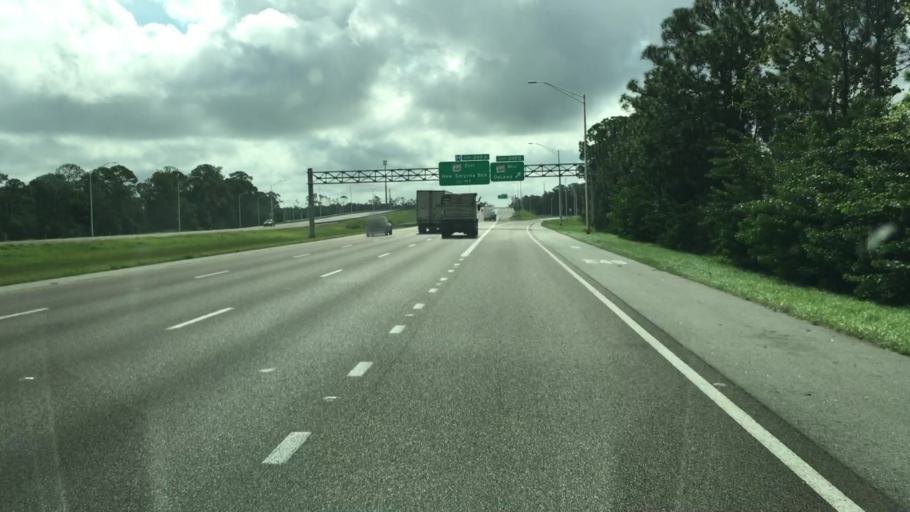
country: US
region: Florida
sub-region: Volusia County
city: Glencoe
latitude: 29.0171
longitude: -80.9910
